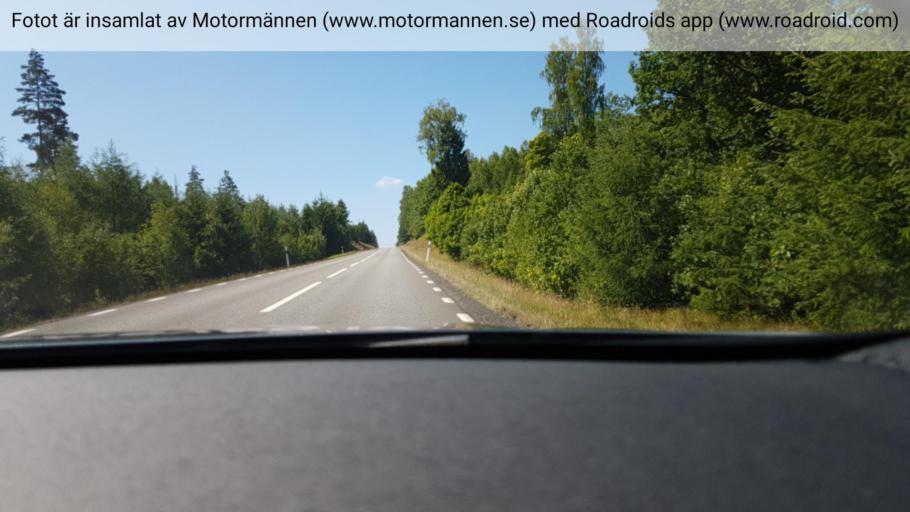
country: SE
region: Joenkoeping
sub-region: Mullsjo Kommun
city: Mullsjoe
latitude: 57.7997
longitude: 13.8475
